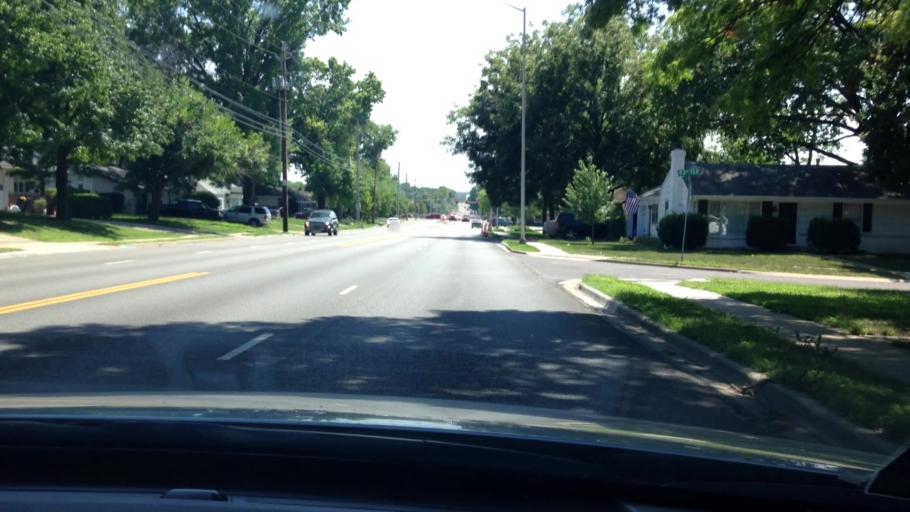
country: US
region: Kansas
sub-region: Johnson County
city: Overland Park
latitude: 38.9593
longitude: -94.6863
